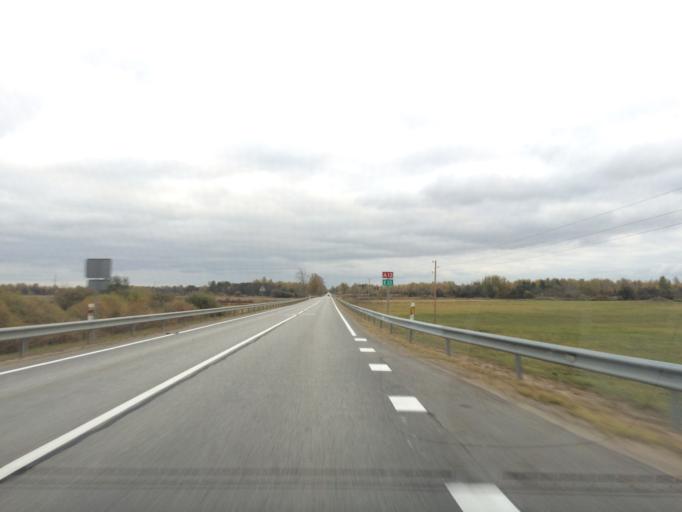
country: LV
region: Livani
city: Livani
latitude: 56.5335
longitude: 26.3232
